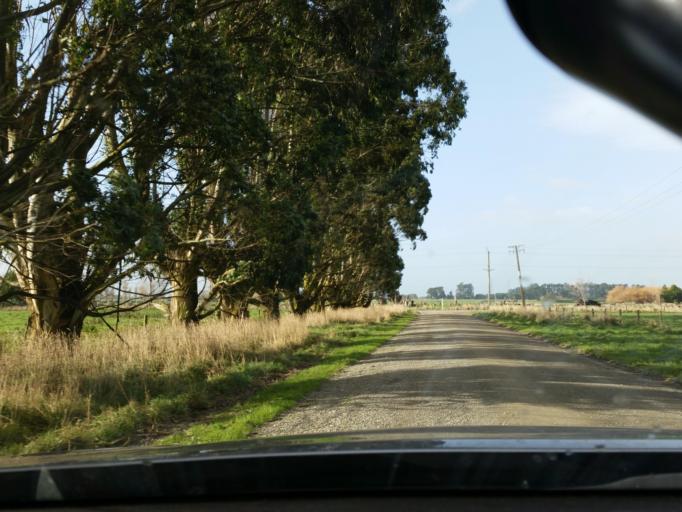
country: NZ
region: Southland
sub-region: Southland District
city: Winton
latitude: -46.2732
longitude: 168.3012
